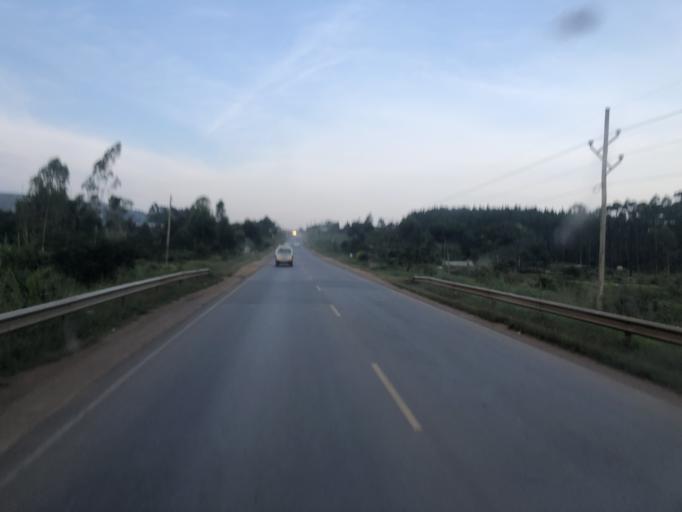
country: UG
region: Central Region
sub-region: Mpigi District
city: Mpigi
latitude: 0.2422
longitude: 32.3596
